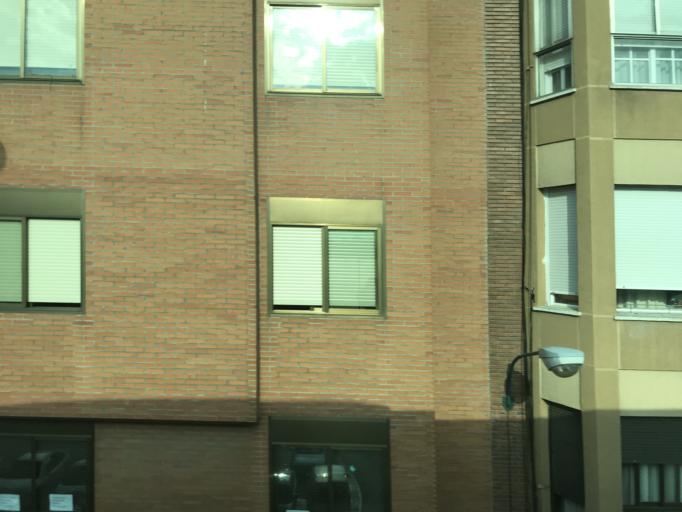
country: ES
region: Castille and Leon
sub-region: Provincia de Valladolid
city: Valladolid
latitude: 41.6402
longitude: -4.7310
